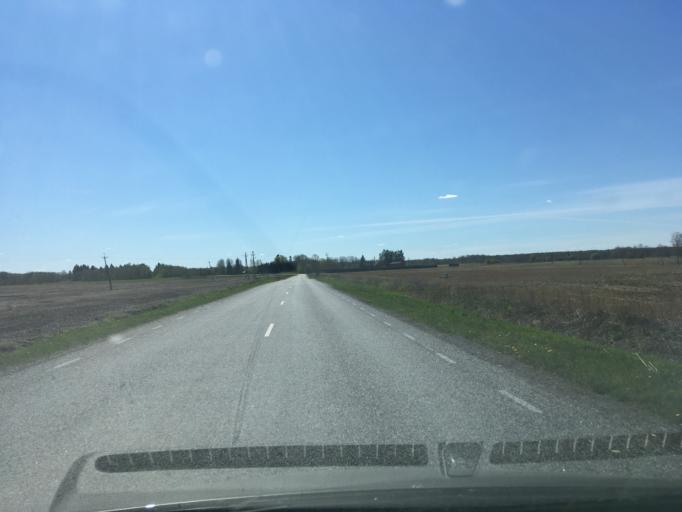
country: EE
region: Harju
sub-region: Raasiku vald
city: Arukula
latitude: 59.4157
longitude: 25.0780
